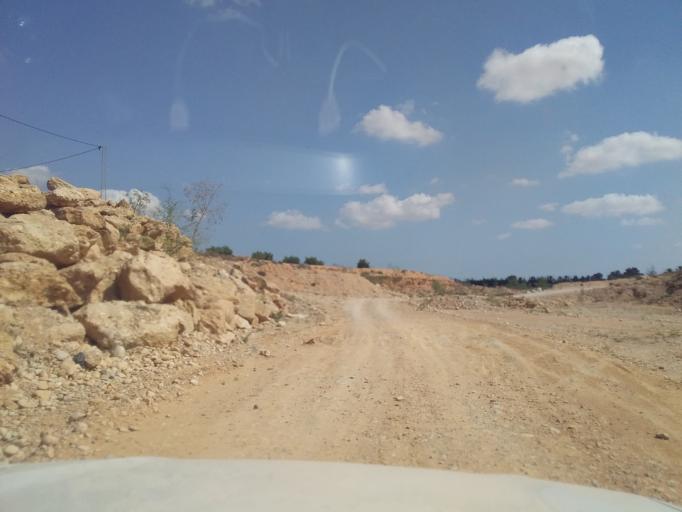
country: TN
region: Madanin
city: Medenine
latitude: 33.6017
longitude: 10.3183
